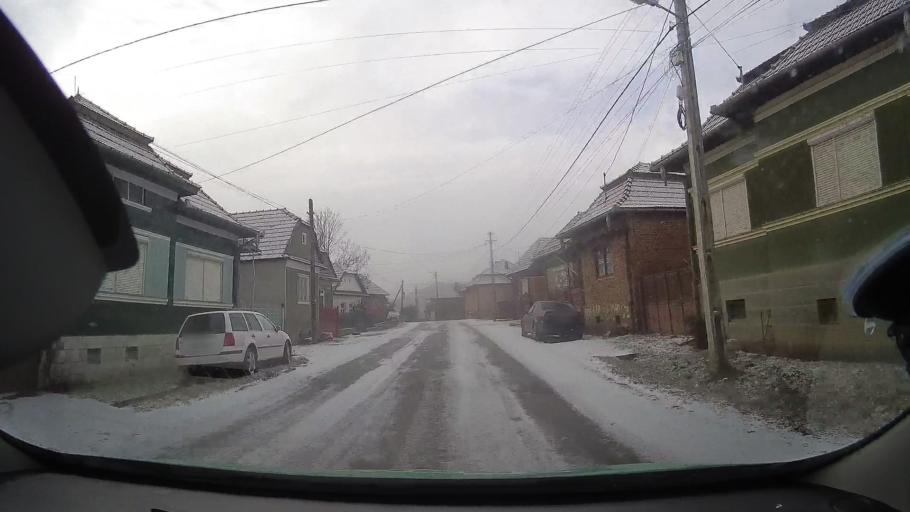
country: RO
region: Alba
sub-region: Comuna Rimetea
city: Rimetea
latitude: 46.4186
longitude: 23.5593
